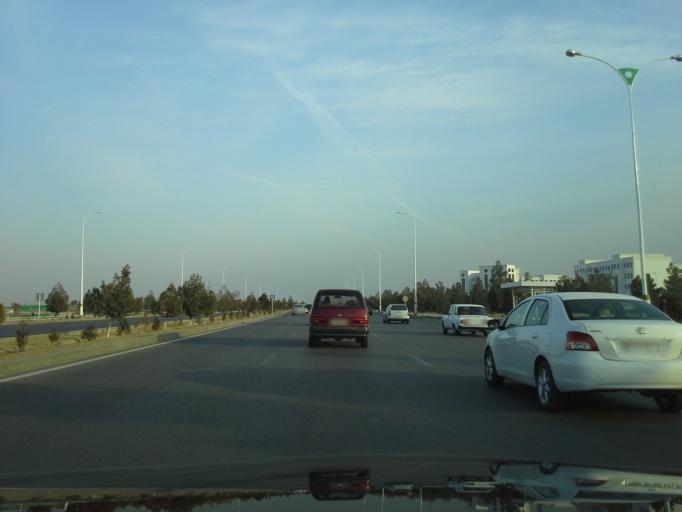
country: TM
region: Ahal
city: Abadan
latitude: 38.0460
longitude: 58.2005
